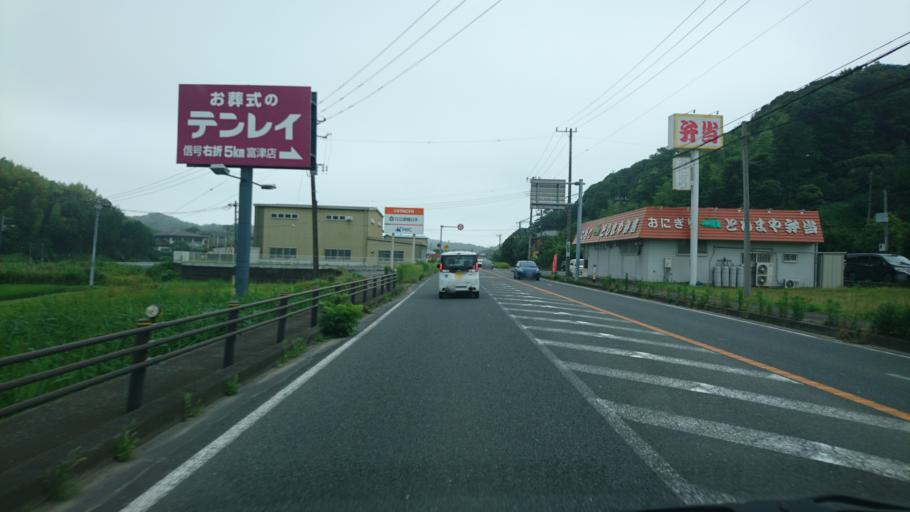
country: JP
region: Chiba
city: Kimitsu
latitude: 35.2665
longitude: 139.8930
